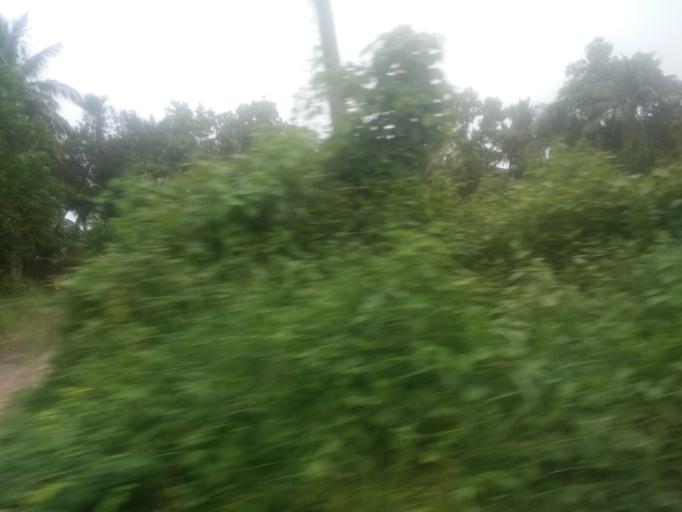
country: IN
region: Goa
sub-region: South Goa
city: Chinchinim
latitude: 15.2142
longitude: 73.9712
